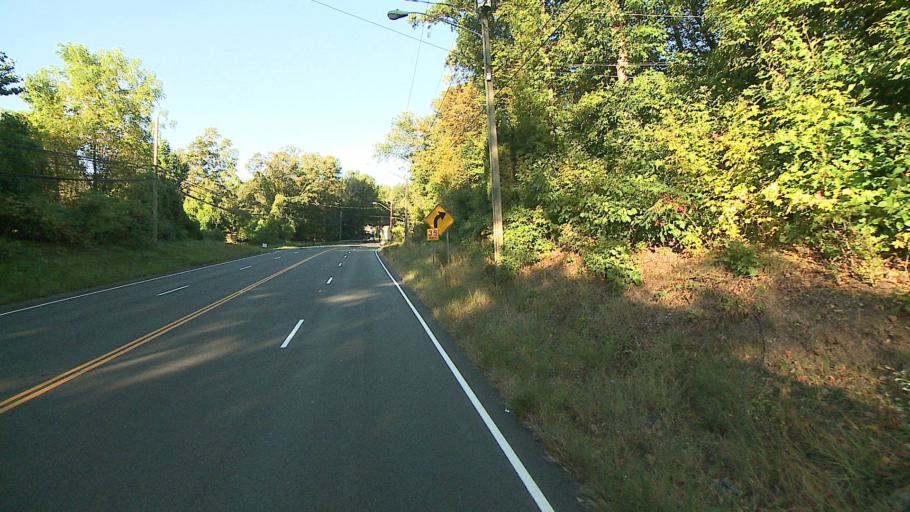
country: US
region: Connecticut
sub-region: Hartford County
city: West Hartford
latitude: 41.7888
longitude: -72.7715
